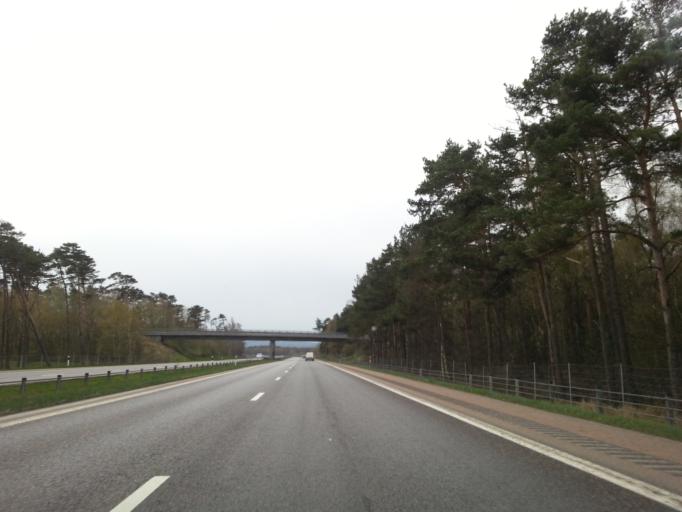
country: SE
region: Halland
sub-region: Laholms Kommun
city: Mellbystrand
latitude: 56.4794
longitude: 12.9459
